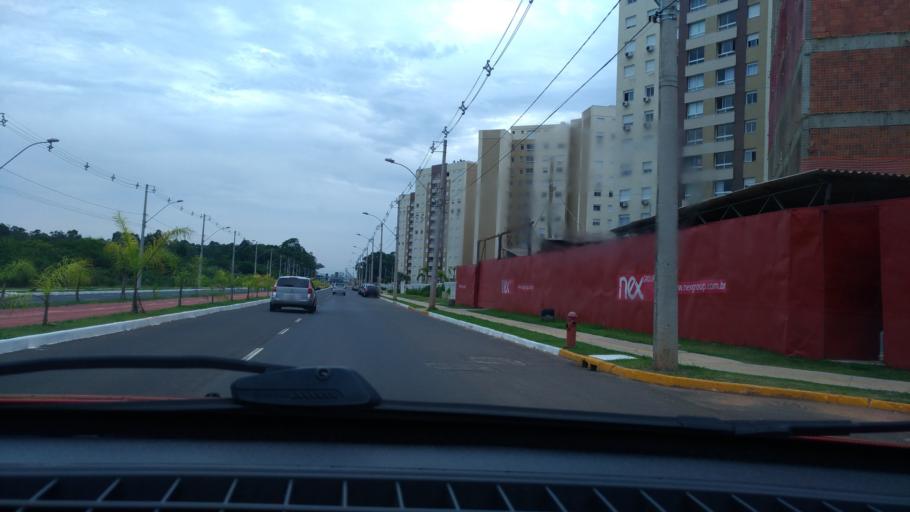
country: BR
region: Rio Grande do Sul
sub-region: Canoas
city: Canoas
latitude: -29.9073
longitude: -51.1651
